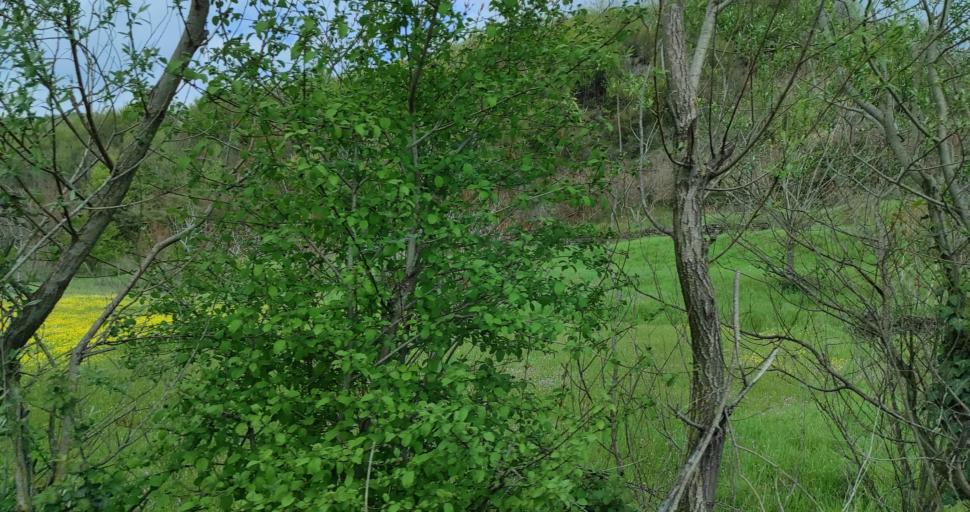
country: AL
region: Shkoder
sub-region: Rrethi i Shkodres
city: Dajc
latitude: 42.0237
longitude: 19.4250
